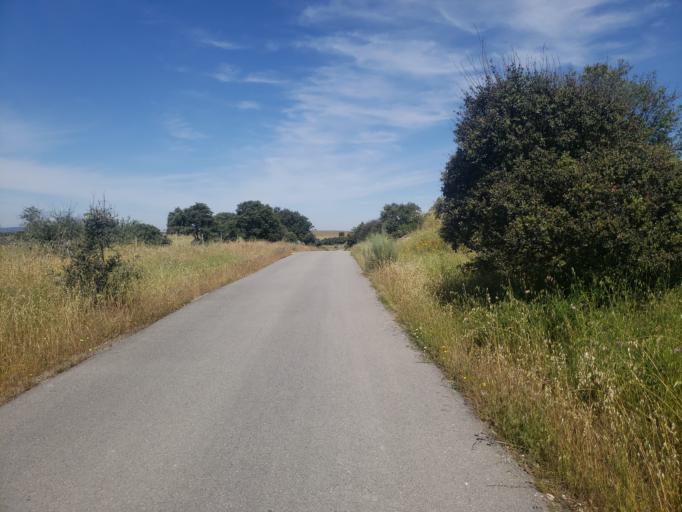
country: ES
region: Extremadura
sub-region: Provincia de Caceres
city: Malpartida de Caceres
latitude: 39.4176
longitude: -6.5028
